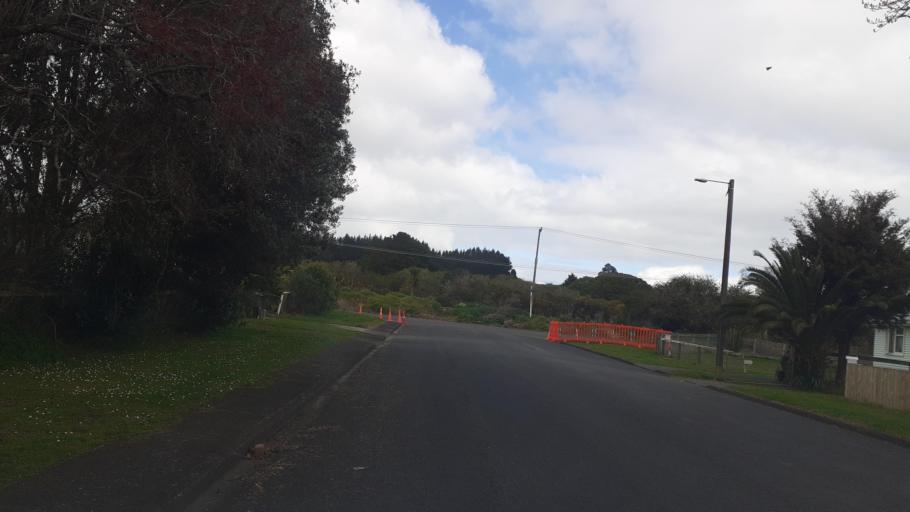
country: NZ
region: Northland
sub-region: Far North District
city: Moerewa
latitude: -35.3903
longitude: 174.0172
